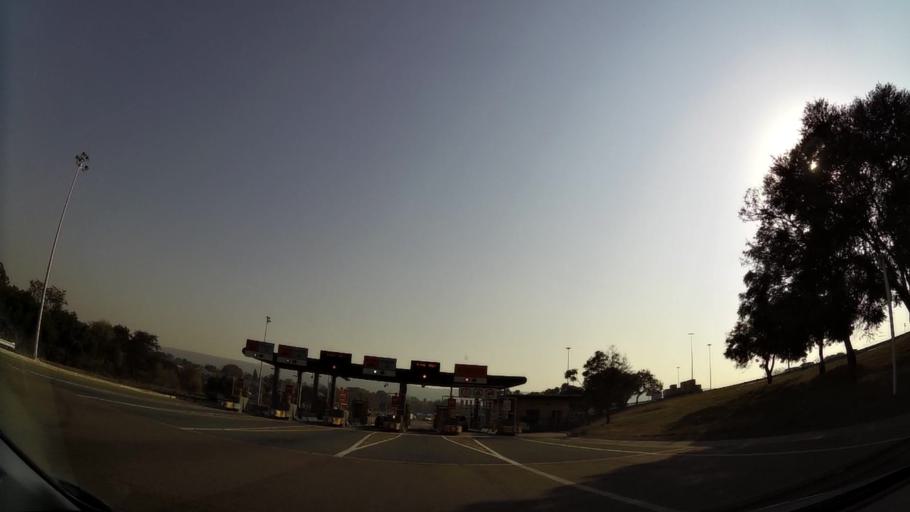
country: ZA
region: Gauteng
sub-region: City of Tshwane Metropolitan Municipality
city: Pretoria
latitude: -25.7129
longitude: 28.2652
